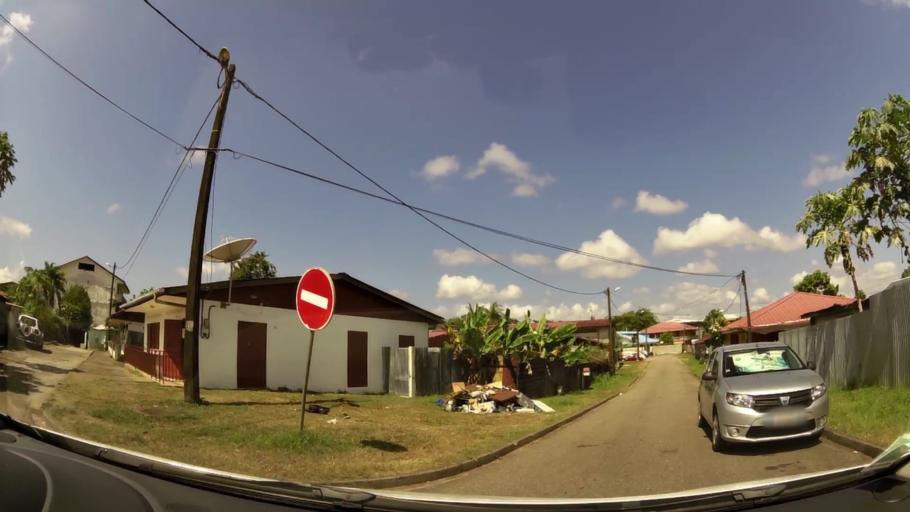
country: GF
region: Guyane
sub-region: Guyane
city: Cayenne
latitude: 4.9219
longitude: -52.3205
